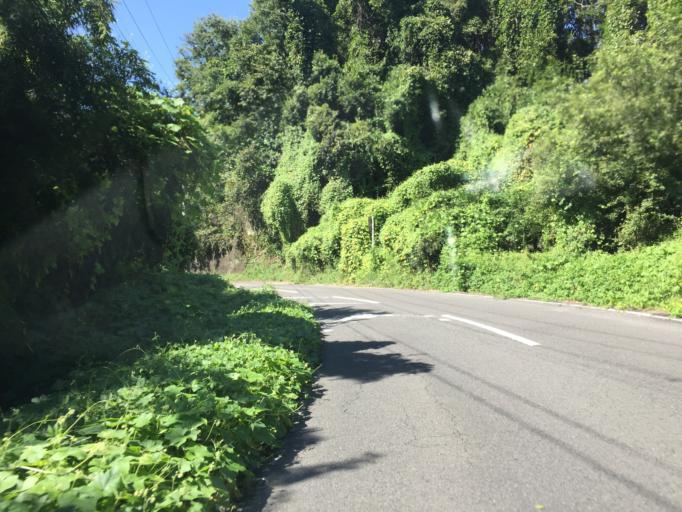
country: JP
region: Fukushima
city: Sukagawa
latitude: 37.2815
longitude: 140.4522
